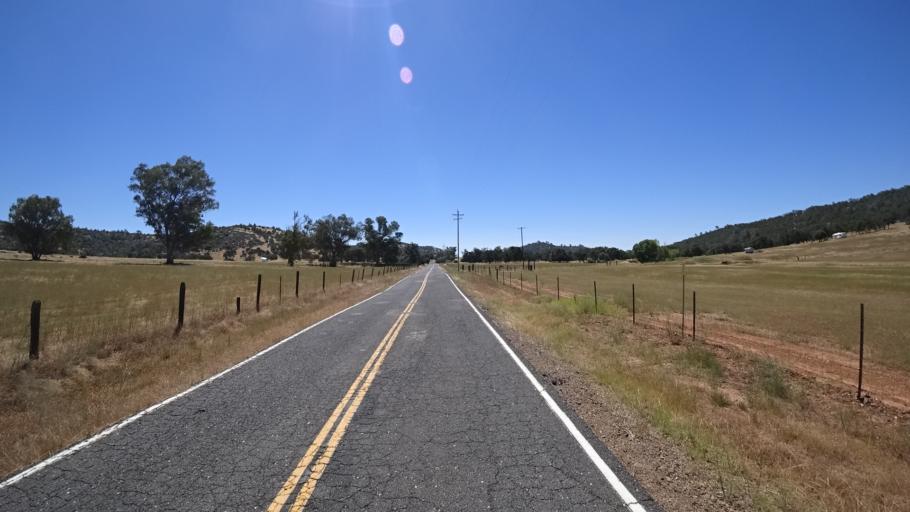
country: US
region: California
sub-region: Calaveras County
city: Copperopolis
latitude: 38.0204
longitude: -120.6827
